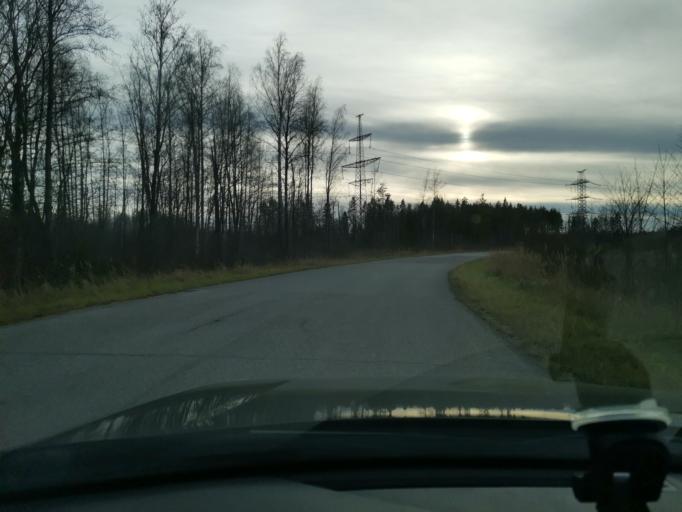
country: EE
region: Ida-Virumaa
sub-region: Sillamaee linn
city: Sillamae
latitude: 59.2700
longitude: 27.9138
